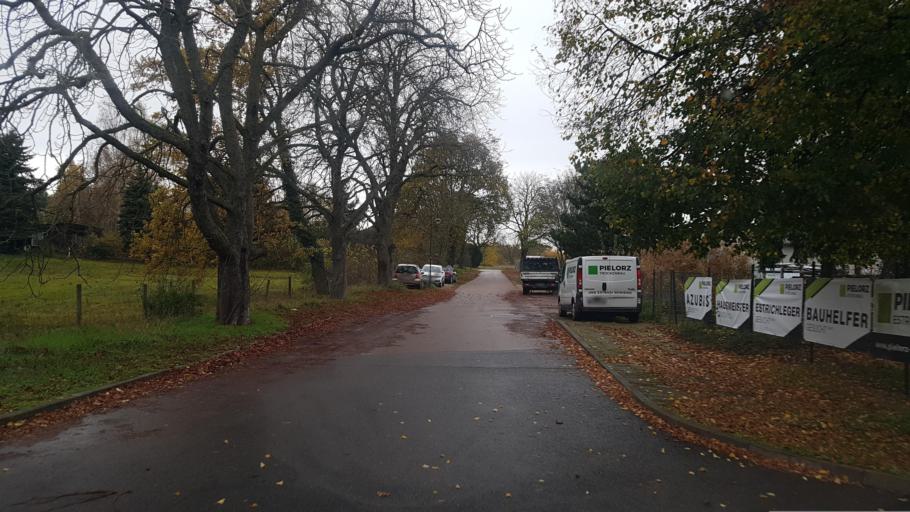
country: DE
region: Saxony-Anhalt
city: Abtsdorf
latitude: 51.8914
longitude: 12.7238
